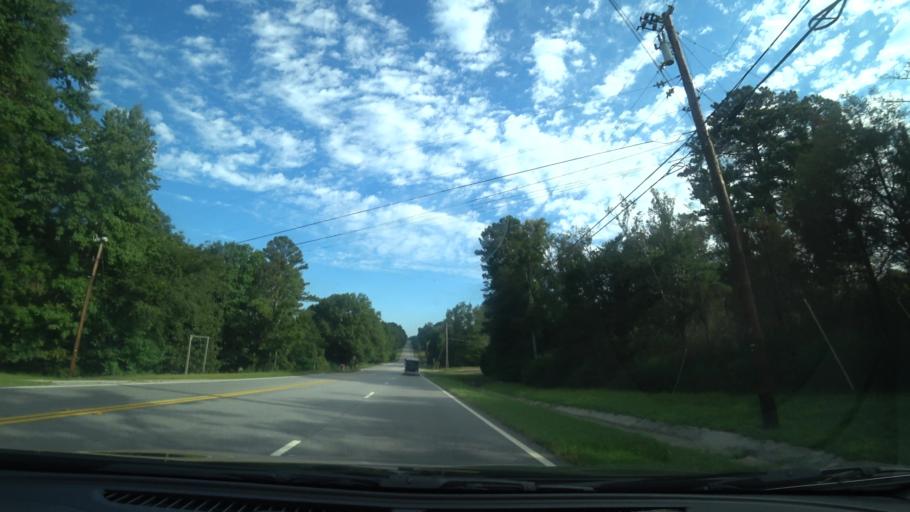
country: US
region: Georgia
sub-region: Rockdale County
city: Lakeview Estates
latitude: 33.7006
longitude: -84.0028
